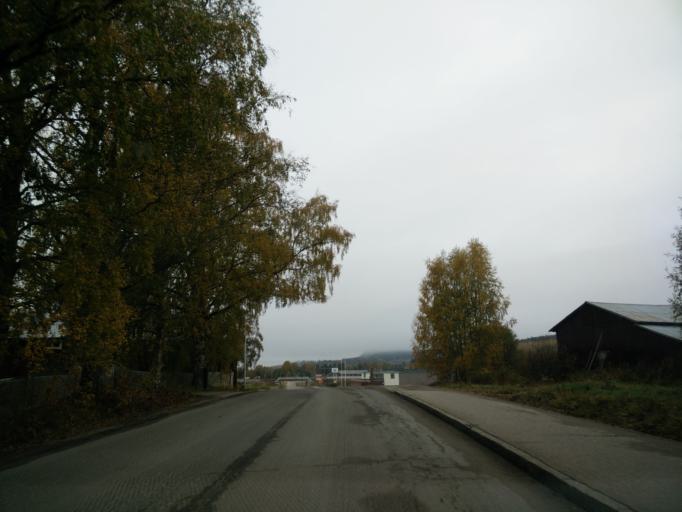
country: SE
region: Vaesternorrland
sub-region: Sundsvalls Kommun
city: Nolby
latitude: 62.2926
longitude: 17.3577
